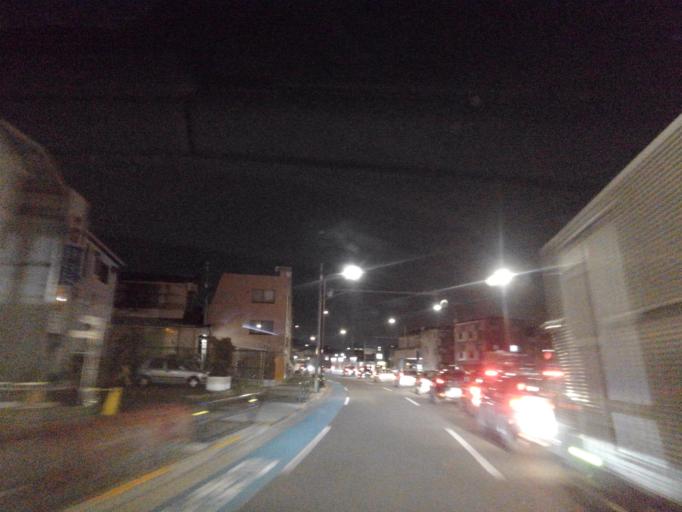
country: JP
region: Tokyo
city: Chofugaoka
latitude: 35.6516
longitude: 139.5370
